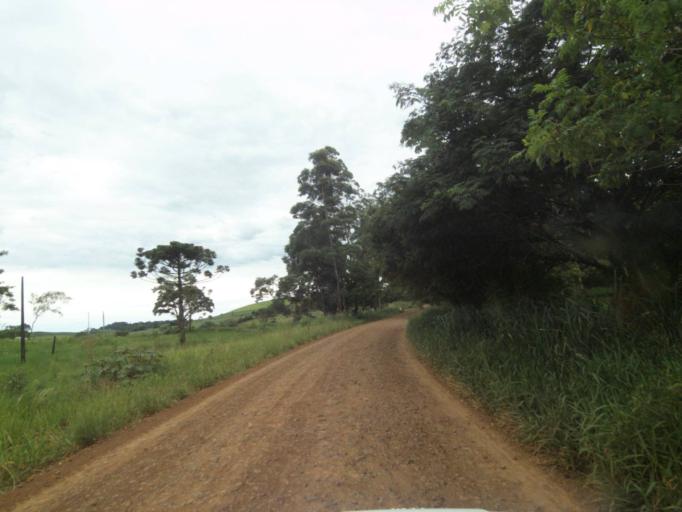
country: BR
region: Parana
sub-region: Guaraniacu
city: Guaraniacu
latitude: -24.9084
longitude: -52.9353
